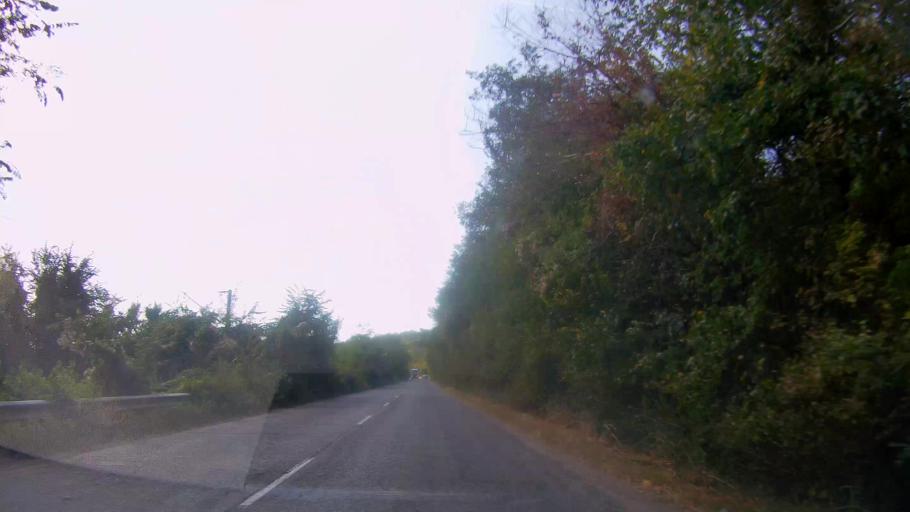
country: BG
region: Veliko Turnovo
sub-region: Obshtina Polski Trumbesh
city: Polski Trumbesh
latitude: 43.4425
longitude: 25.6555
